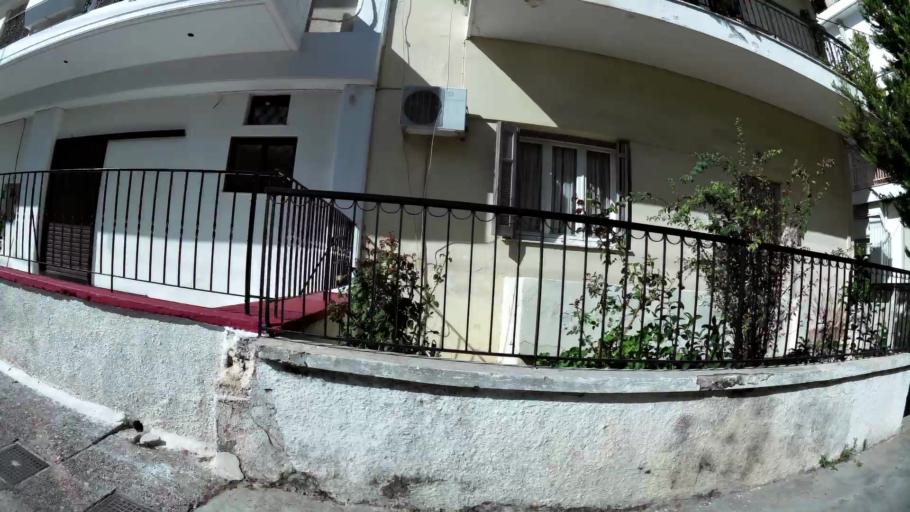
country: GR
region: Attica
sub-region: Nomarchia Athinas
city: Cholargos
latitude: 38.0088
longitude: 23.7942
